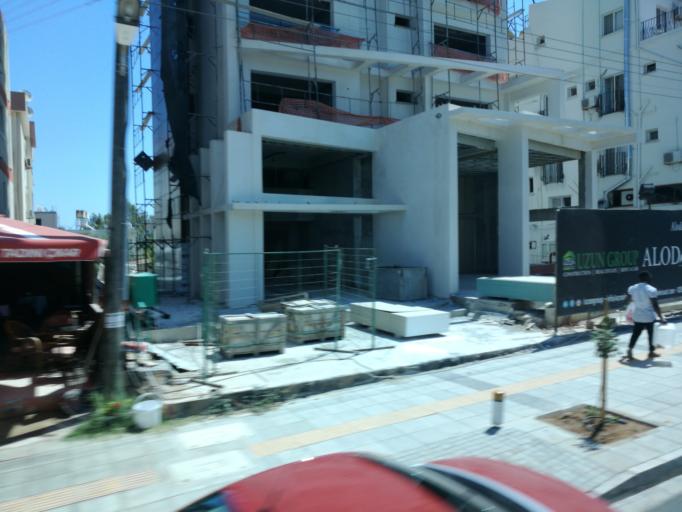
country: CY
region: Ammochostos
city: Famagusta
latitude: 35.1443
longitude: 33.9127
